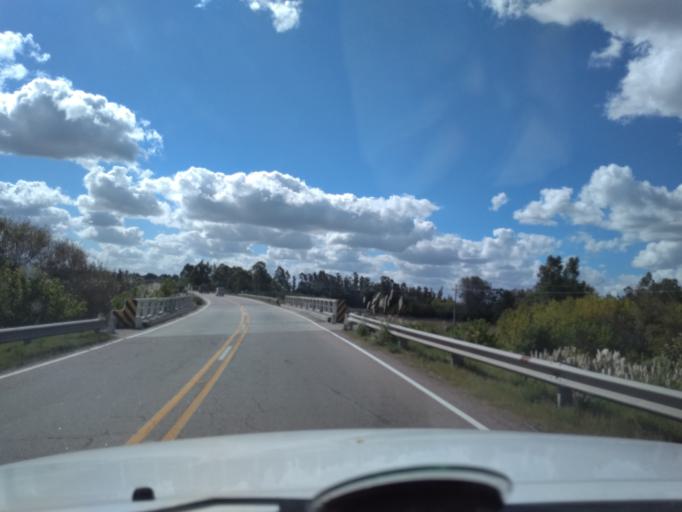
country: UY
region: Canelones
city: Sauce
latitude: -34.6740
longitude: -56.0515
